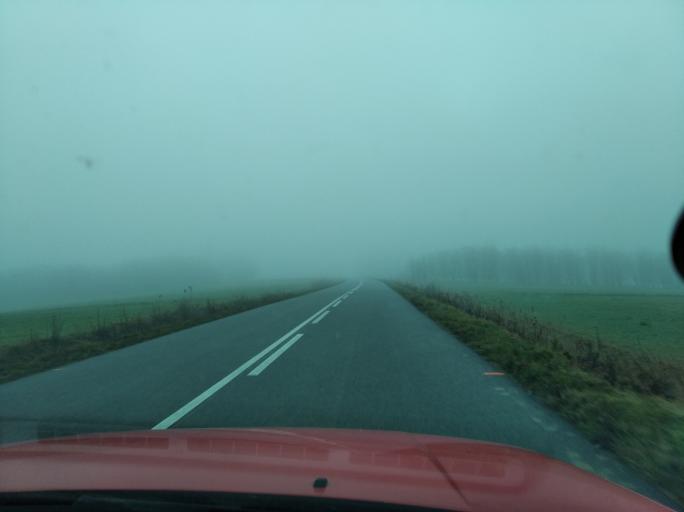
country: PL
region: Subcarpathian Voivodeship
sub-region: Powiat jaroslawski
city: Jodlowka
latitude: 49.8826
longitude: 22.4580
